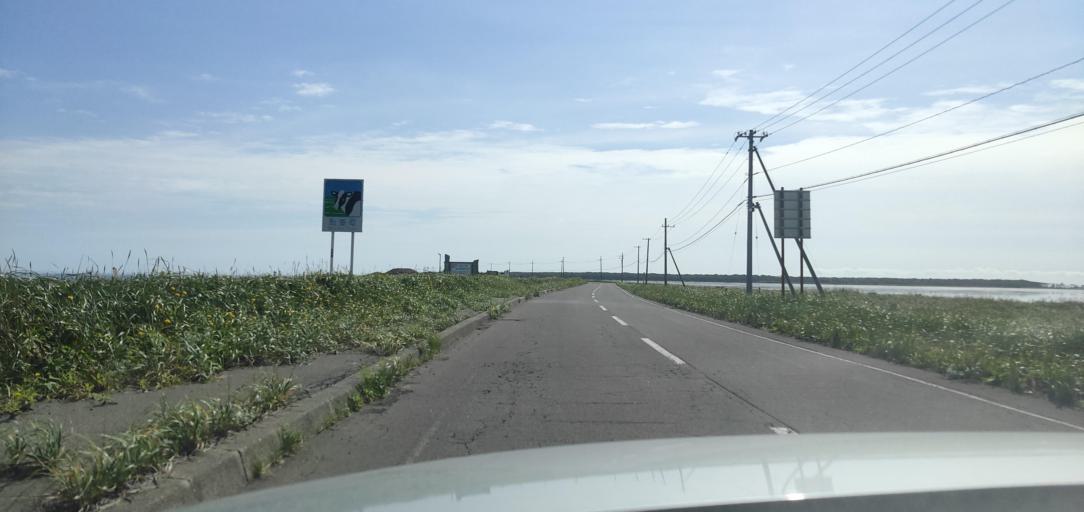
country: JP
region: Hokkaido
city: Shibetsu
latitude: 43.6146
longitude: 145.2456
